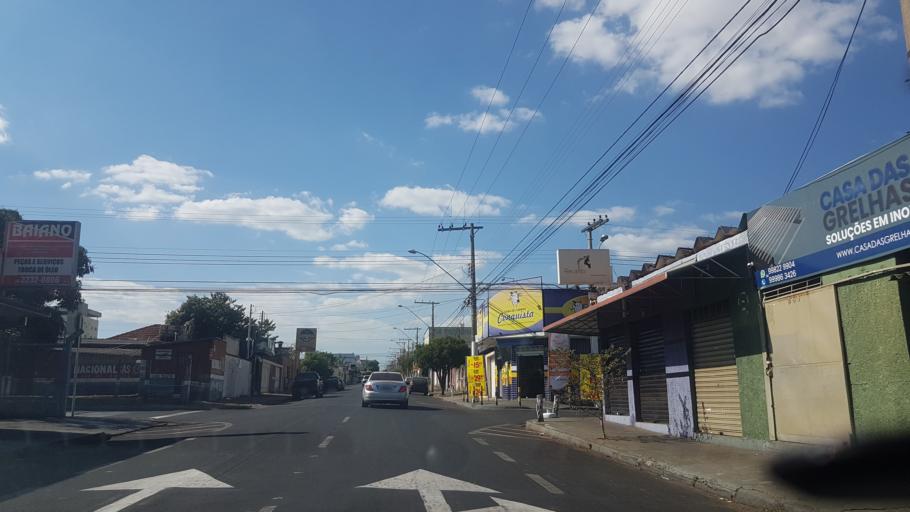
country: BR
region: Minas Gerais
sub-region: Uberlandia
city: Uberlandia
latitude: -18.8959
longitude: -48.2679
